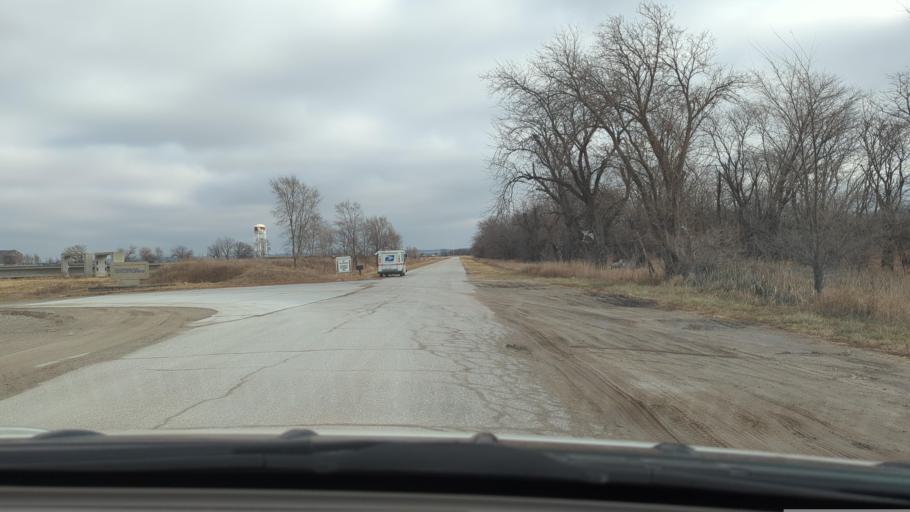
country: US
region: Nebraska
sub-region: Sarpy County
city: Offutt Air Force Base
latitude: 41.0687
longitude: -95.9201
